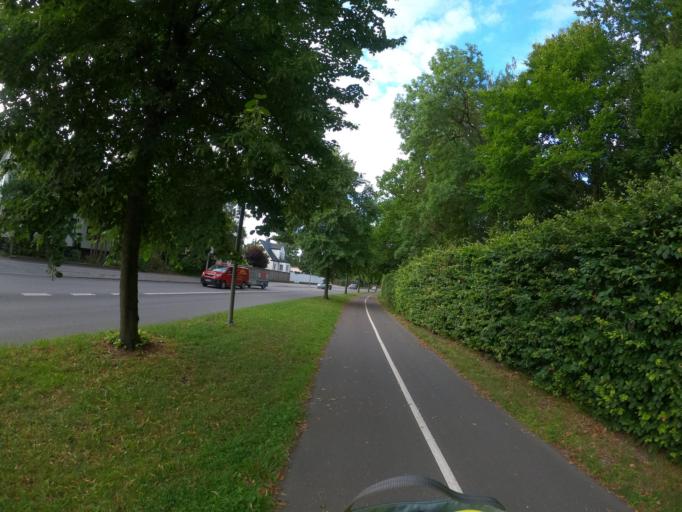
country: SE
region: Skane
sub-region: Lunds Kommun
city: Lund
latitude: 55.6868
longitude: 13.1868
